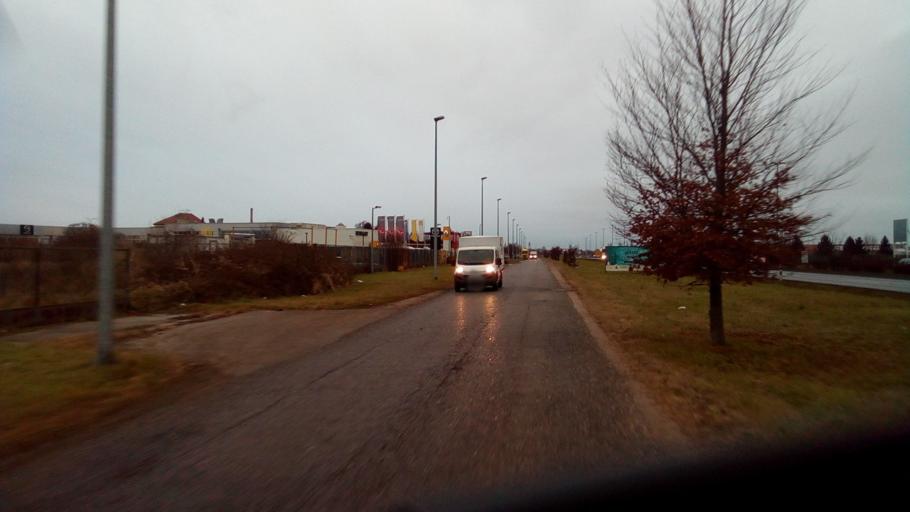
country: HR
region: Varazdinska
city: Varazdin
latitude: 46.2857
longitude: 16.3546
